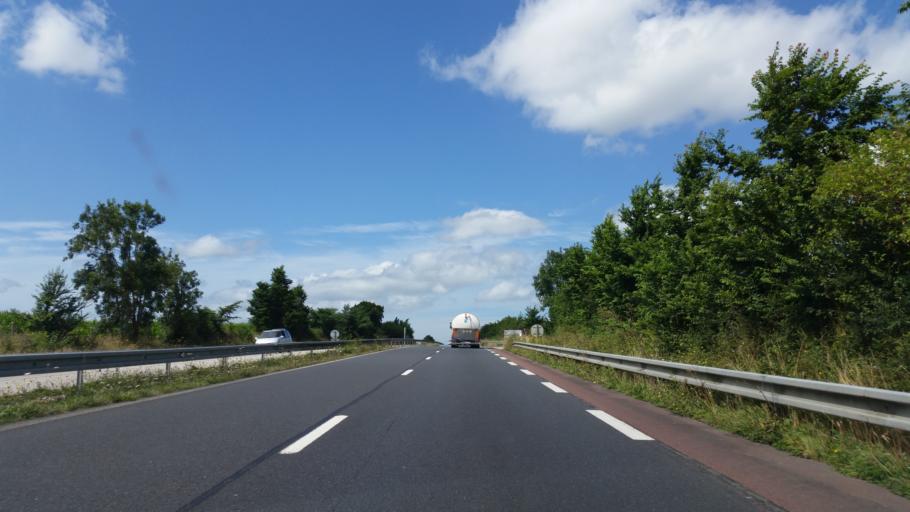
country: FR
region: Lower Normandy
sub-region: Departement de la Manche
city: Montebourg
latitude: 49.4525
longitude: -1.3514
